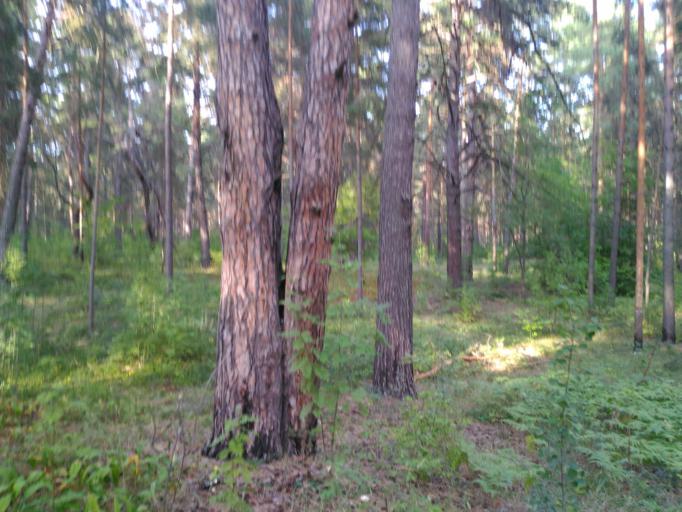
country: RU
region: Ulyanovsk
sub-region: Ulyanovskiy Rayon
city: Ulyanovsk
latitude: 54.3536
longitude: 48.5201
